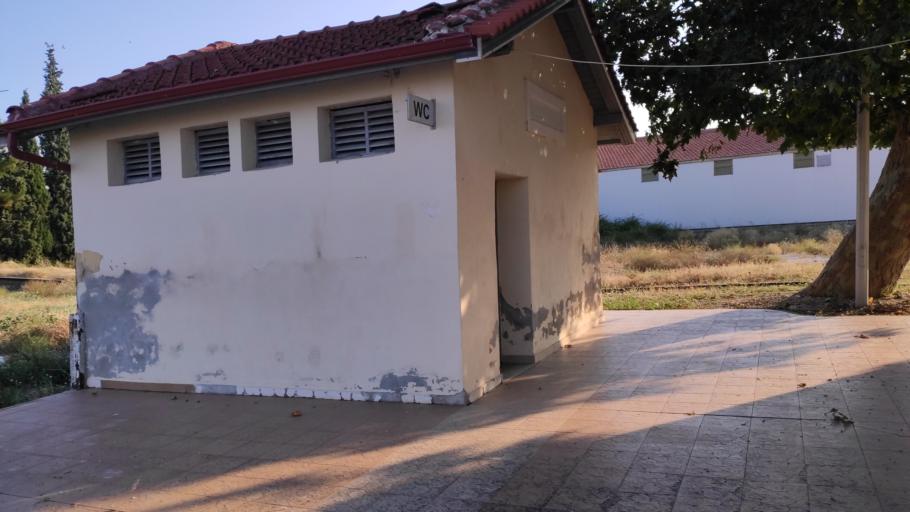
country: GR
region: Central Macedonia
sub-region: Nomos Serron
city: Charopo
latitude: 41.2625
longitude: 23.3452
